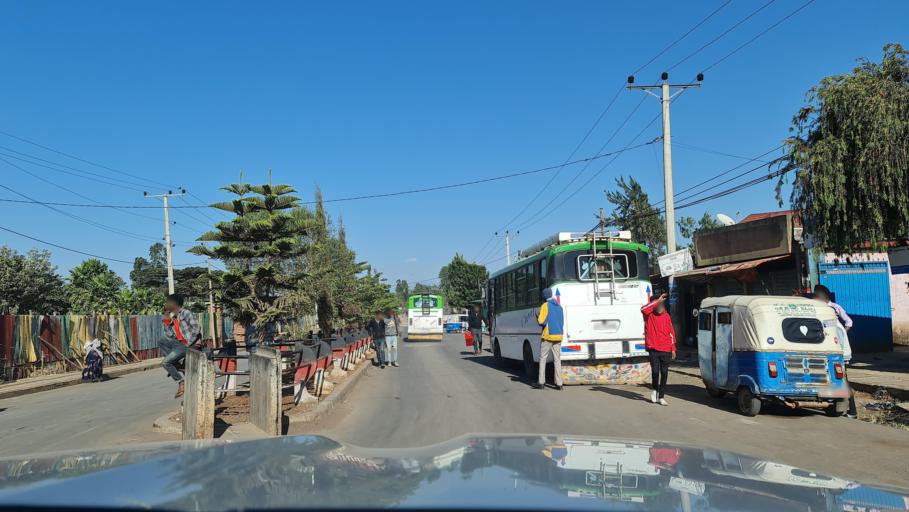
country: ET
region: Oromiya
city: Waliso
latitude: 8.5426
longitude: 37.9704
